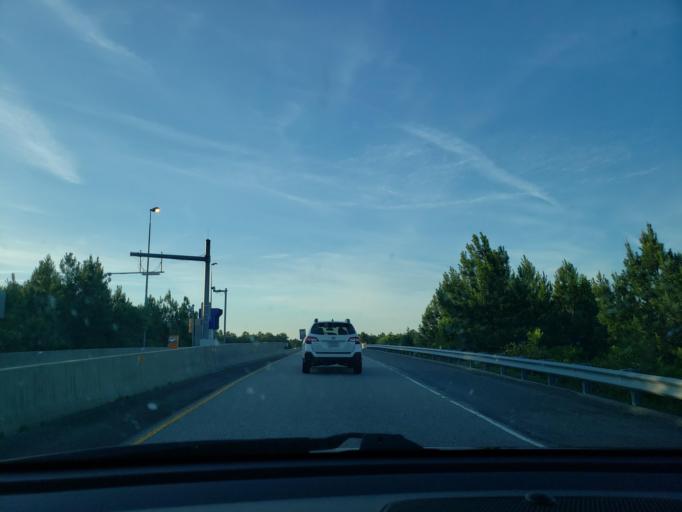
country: US
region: Virginia
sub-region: Henrico County
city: Fort Lee
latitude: 37.4777
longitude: -77.3398
